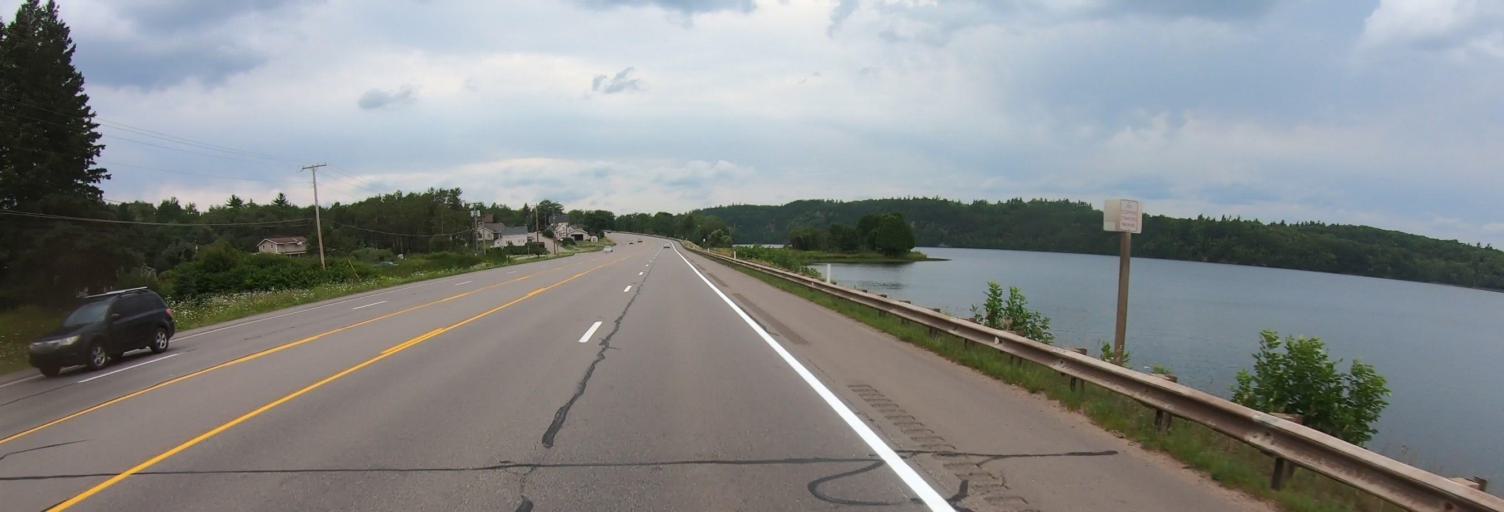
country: US
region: Michigan
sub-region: Marquette County
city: Negaunee
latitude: 46.5102
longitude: -87.6320
